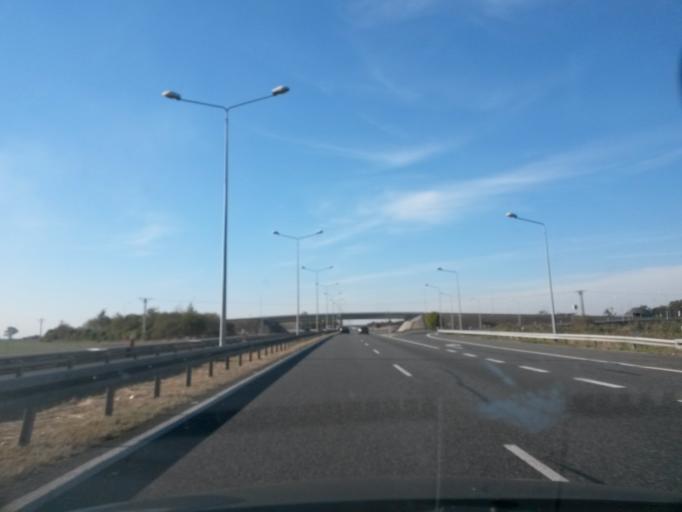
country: PL
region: Opole Voivodeship
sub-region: Powiat brzeski
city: Grodkow
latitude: 50.7795
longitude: 17.3535
